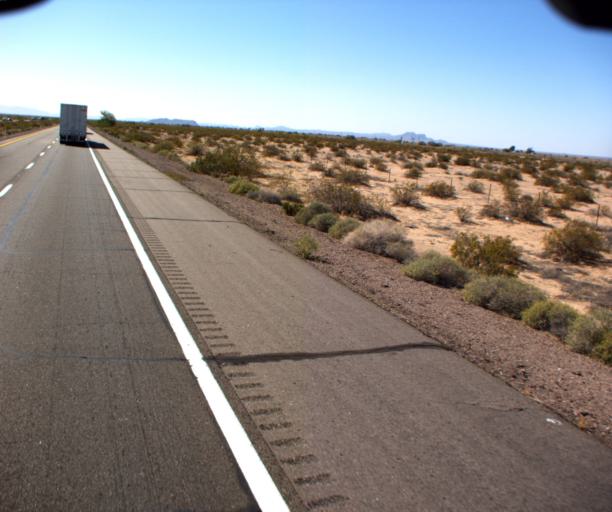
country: US
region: Arizona
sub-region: Yuma County
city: Wellton
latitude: 32.7099
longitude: -113.8466
